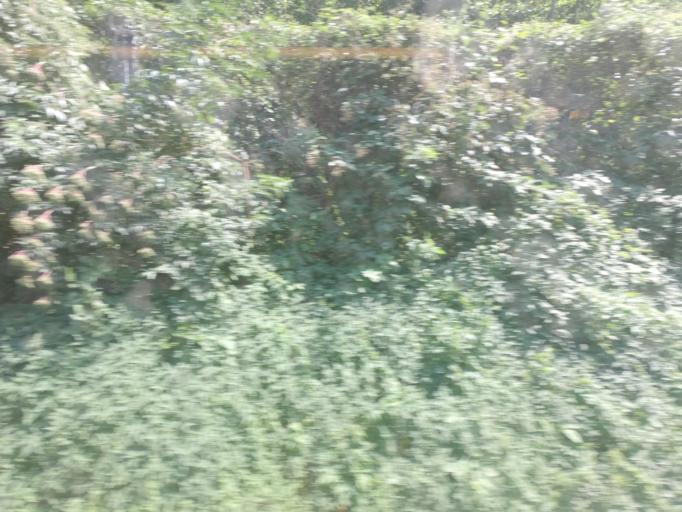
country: CH
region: Valais
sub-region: Martigny District
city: Martigny-Combe
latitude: 46.0885
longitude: 7.0617
